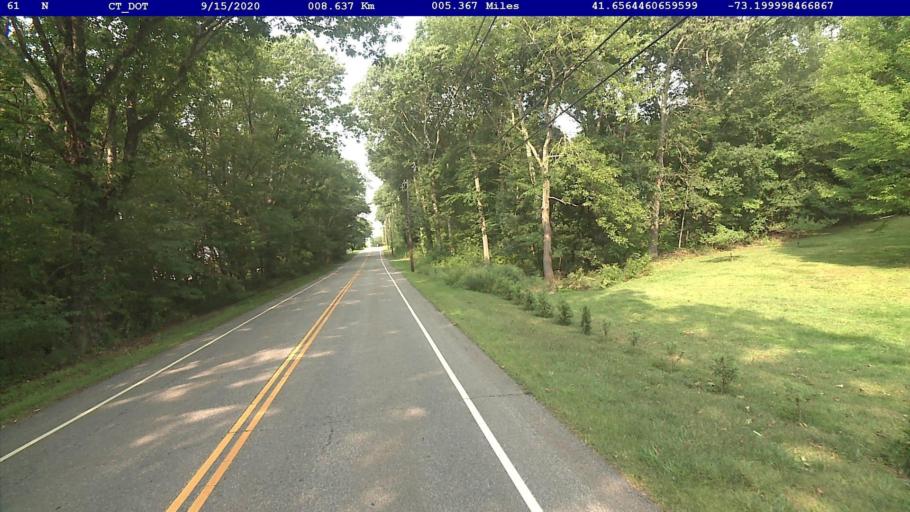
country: US
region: Connecticut
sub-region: Litchfield County
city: Bethlehem Village
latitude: 41.6565
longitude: -73.2000
